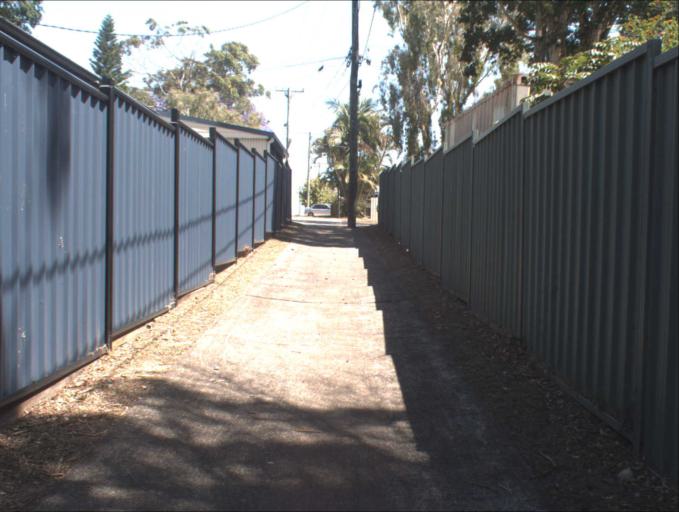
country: AU
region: Queensland
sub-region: Logan
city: Rochedale South
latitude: -27.5968
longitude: 153.1285
